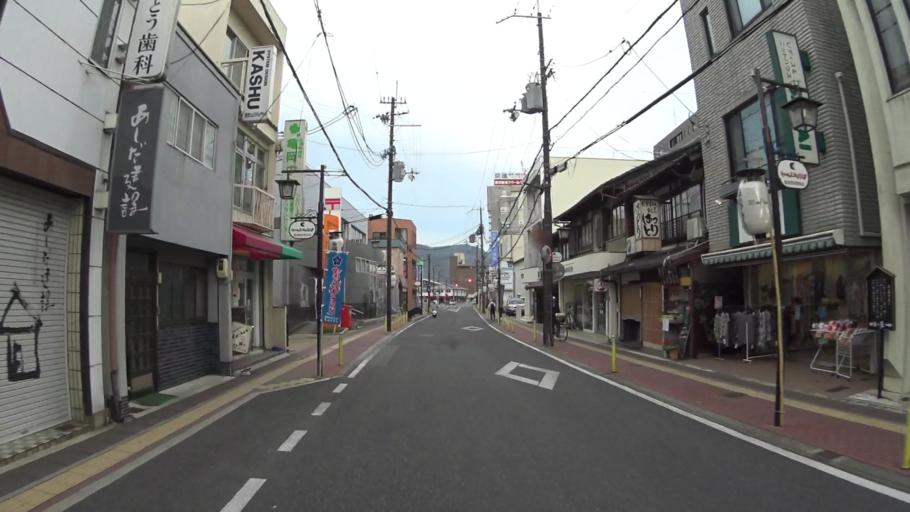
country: JP
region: Kyoto
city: Kameoka
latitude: 35.0165
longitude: 135.5805
